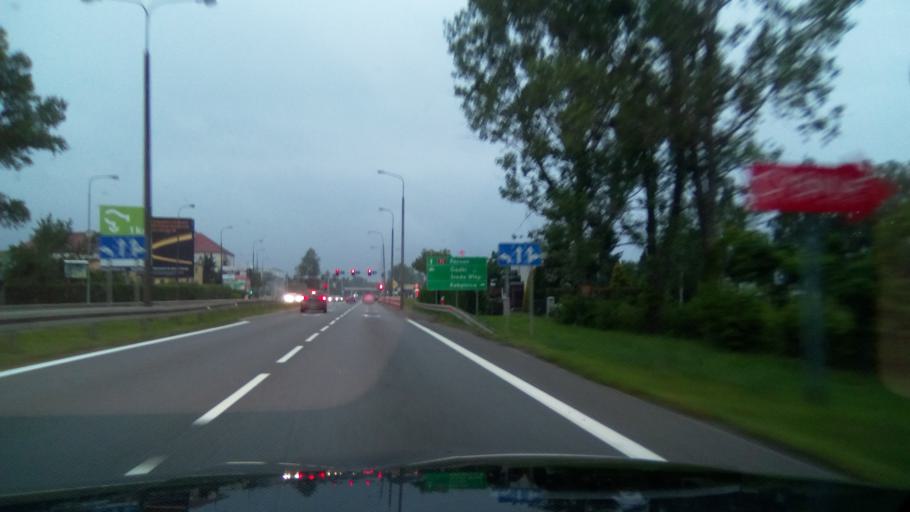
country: PL
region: Greater Poland Voivodeship
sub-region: Powiat poznanski
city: Swarzedz
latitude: 52.4065
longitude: 17.0868
